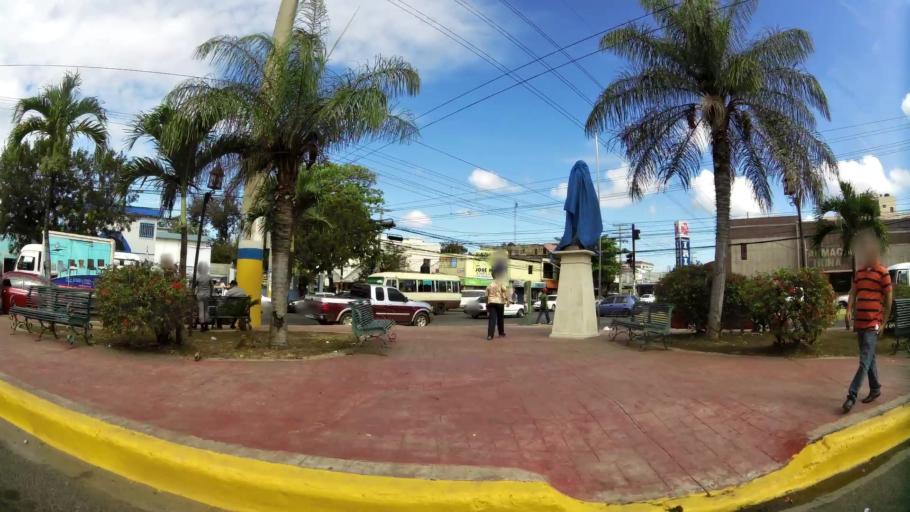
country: DO
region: Santo Domingo
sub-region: Santo Domingo
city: Santo Domingo Este
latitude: 18.4942
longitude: -69.8649
